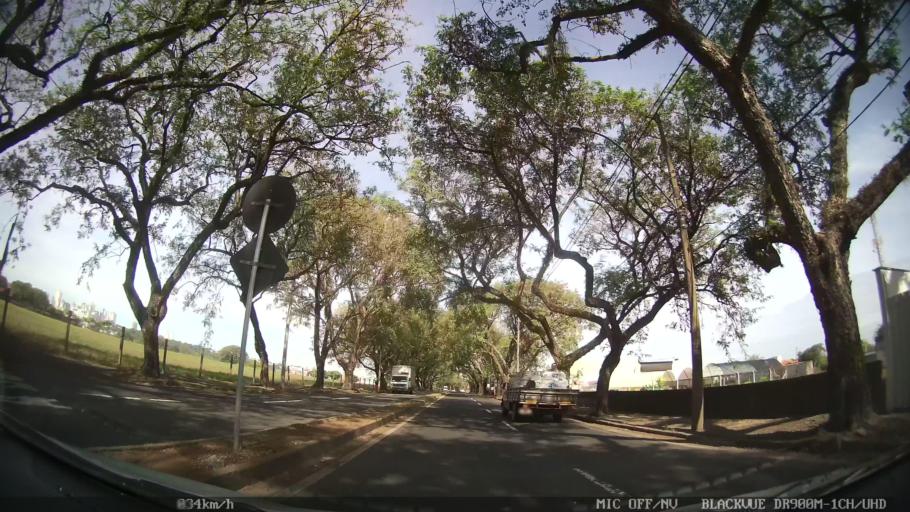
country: BR
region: Sao Paulo
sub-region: Piracicaba
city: Piracicaba
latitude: -22.7184
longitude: -47.6622
